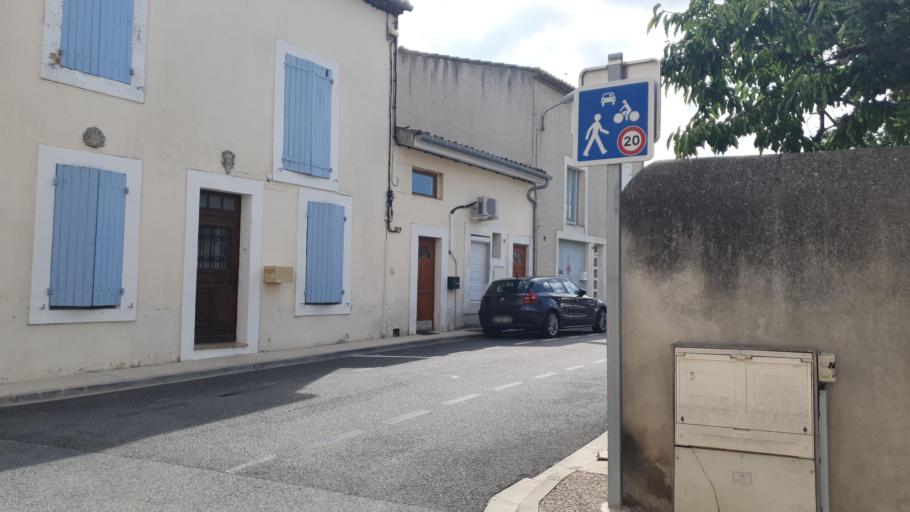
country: FR
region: Languedoc-Roussillon
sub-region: Departement de l'Aude
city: Bram
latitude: 43.2421
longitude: 2.1150
